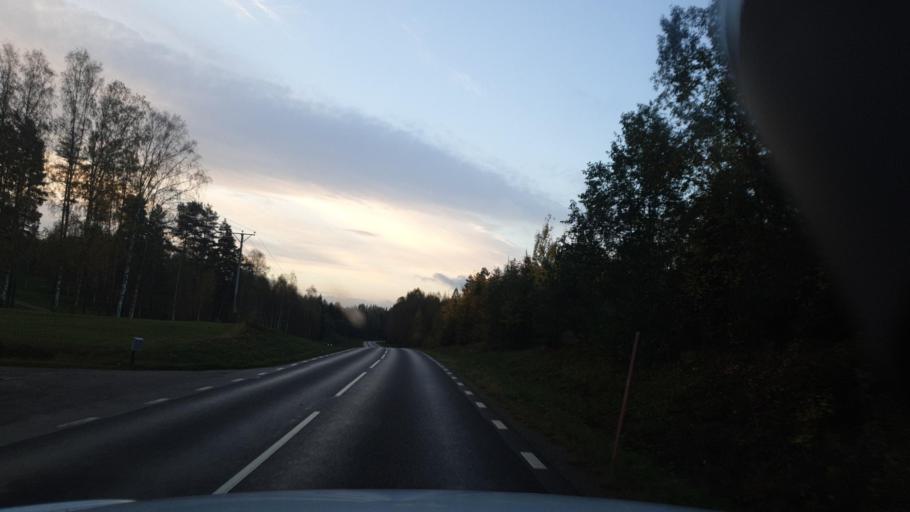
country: SE
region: Vaermland
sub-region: Arvika Kommun
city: Arvika
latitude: 59.7275
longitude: 12.5646
